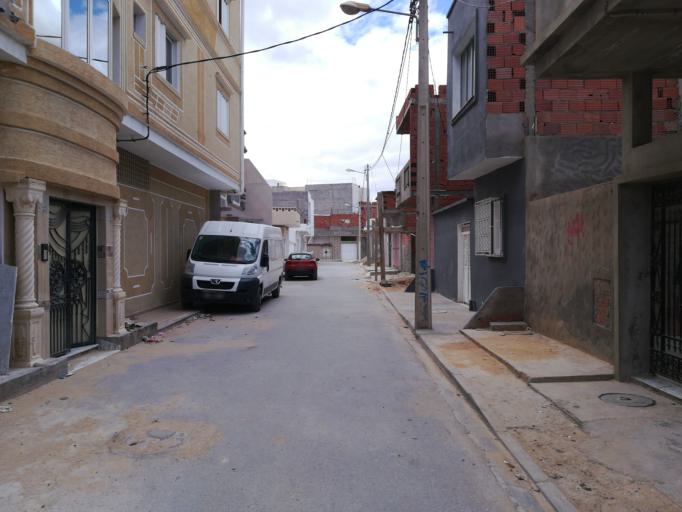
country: TN
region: Al Qayrawan
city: Kairouan
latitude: 35.6656
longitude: 10.0851
